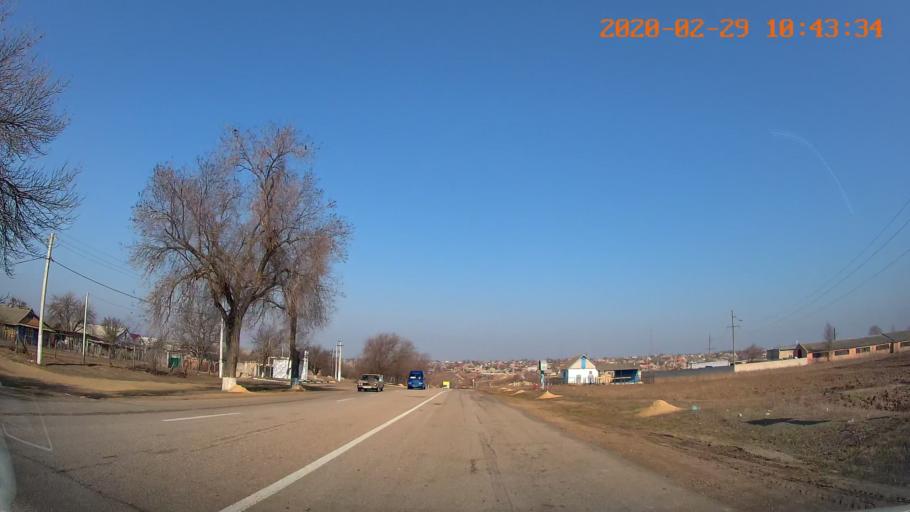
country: MD
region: Telenesti
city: Grigoriopol
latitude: 47.0628
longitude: 29.4028
